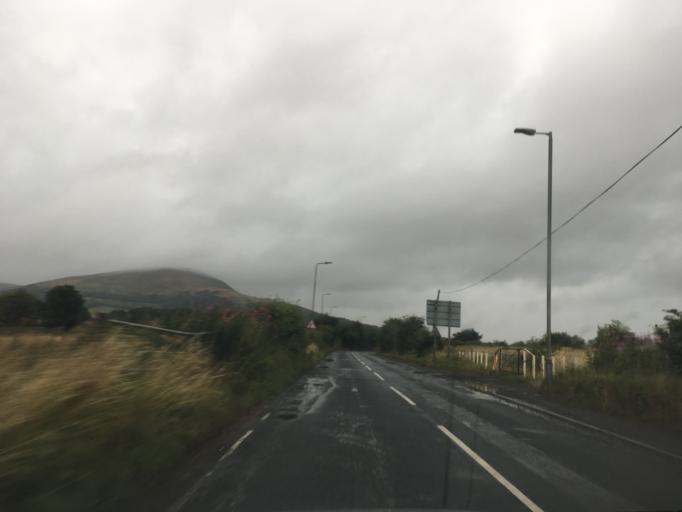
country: GB
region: Scotland
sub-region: Midlothian
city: Loanhead
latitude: 55.8799
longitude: -3.1727
